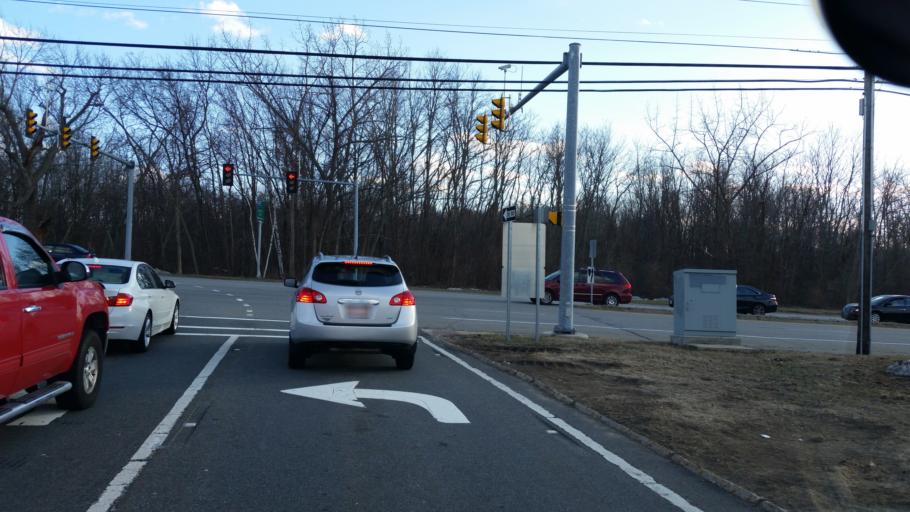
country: US
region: Massachusetts
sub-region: Essex County
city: Haverhill
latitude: 42.7840
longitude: -71.1174
